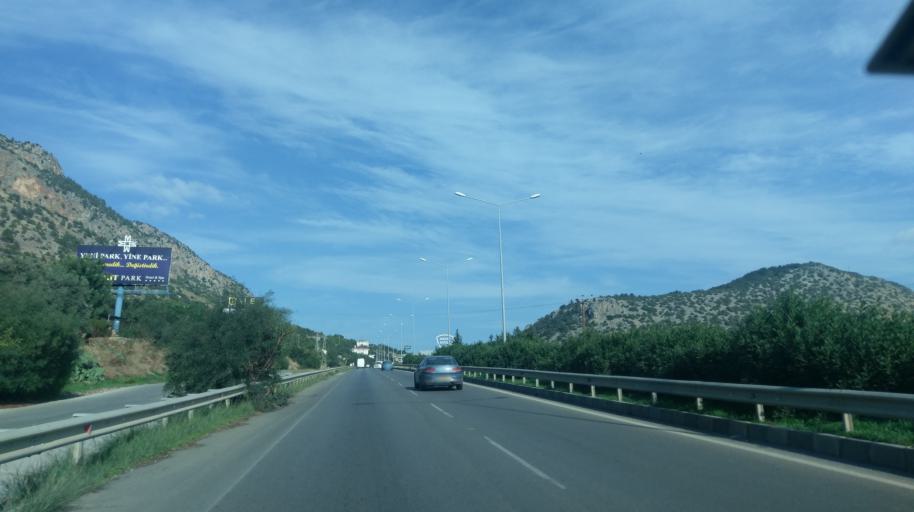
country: CY
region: Keryneia
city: Kyrenia
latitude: 35.2970
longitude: 33.2794
